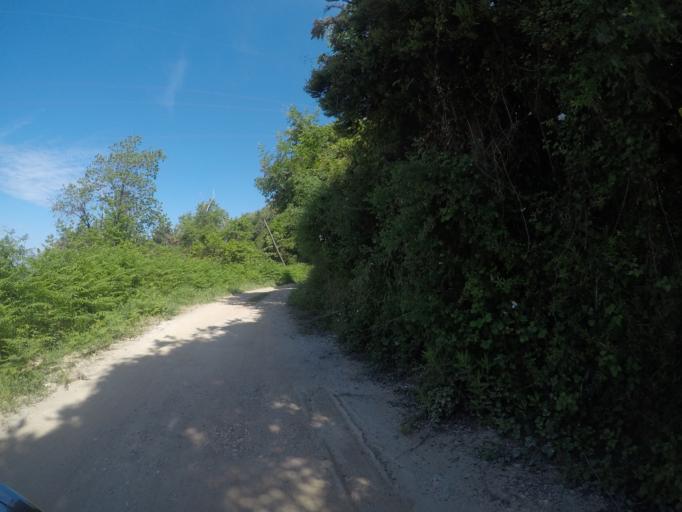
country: IT
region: Tuscany
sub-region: Provincia di Massa-Carrara
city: Carrara
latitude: 44.0614
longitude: 10.1017
